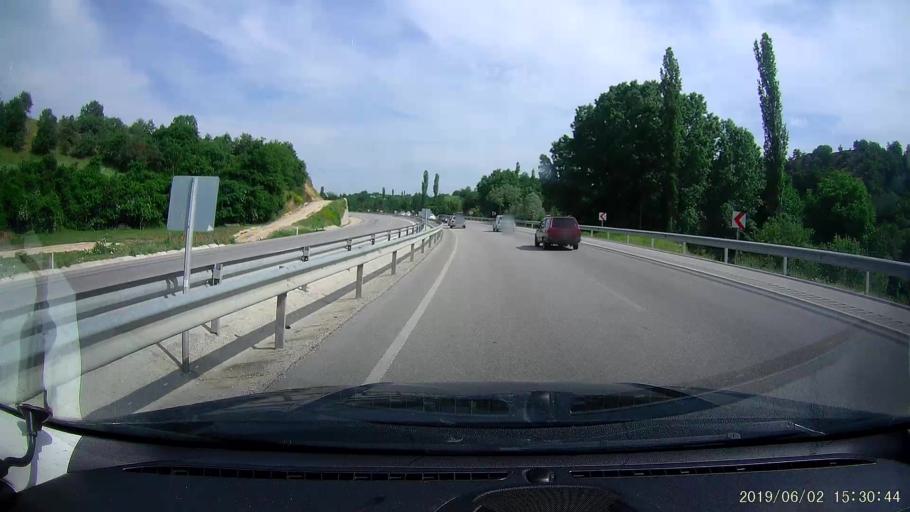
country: TR
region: Amasya
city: Saraycik
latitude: 40.9503
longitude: 35.1144
